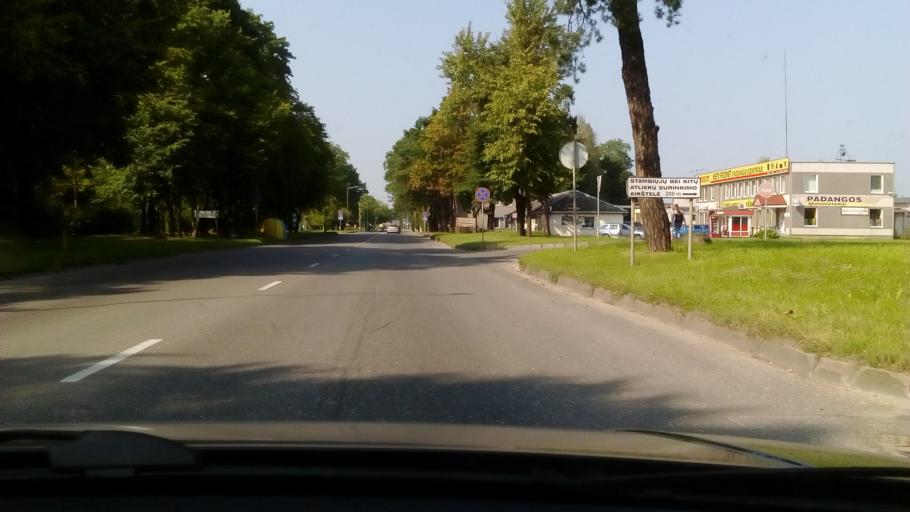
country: LT
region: Alytaus apskritis
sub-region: Alytus
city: Alytus
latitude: 54.3845
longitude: 24.0494
